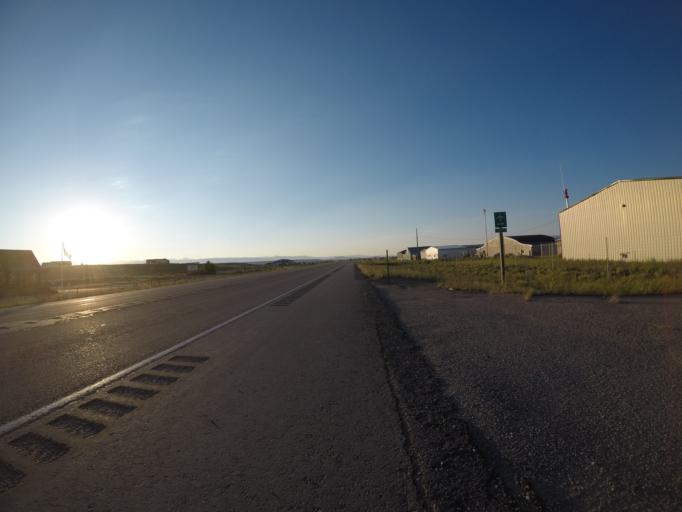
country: US
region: Wyoming
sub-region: Sublette County
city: Pinedale
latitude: 42.7996
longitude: -109.8055
